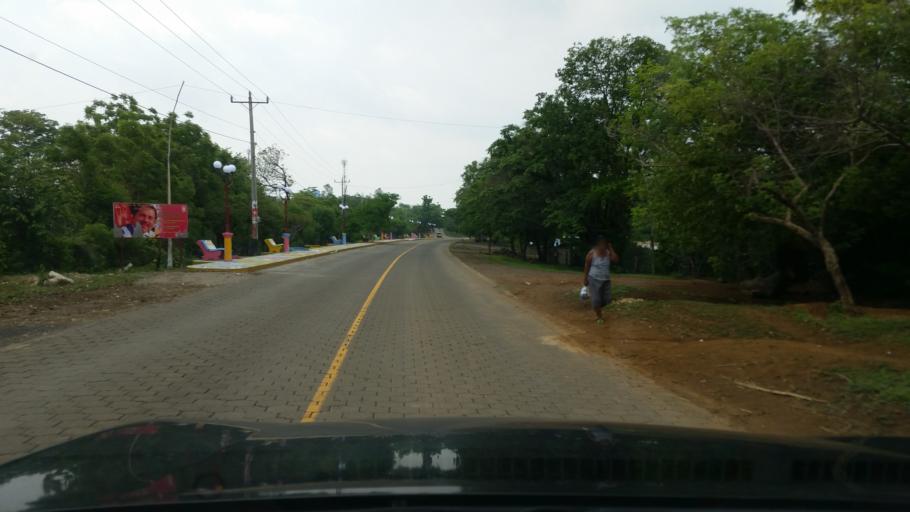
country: NI
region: Managua
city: Carlos Fonseca Amador
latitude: 11.8954
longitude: -86.5135
